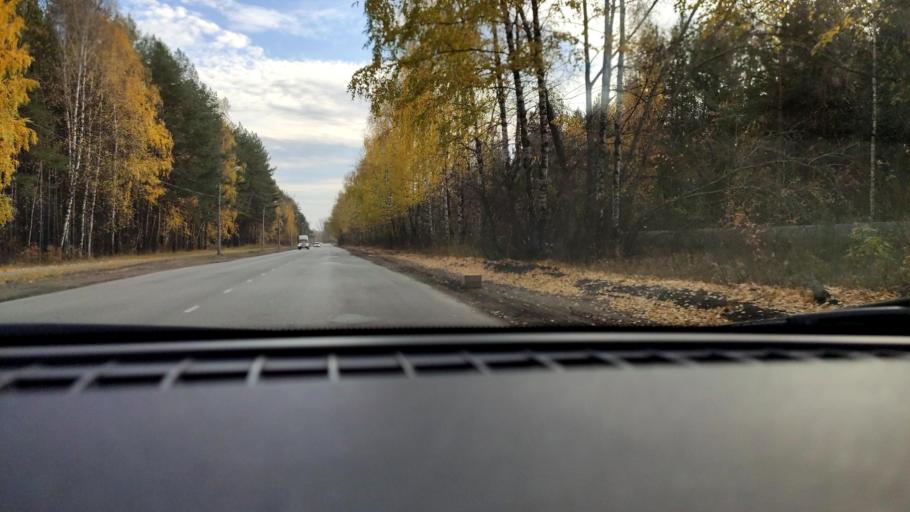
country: RU
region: Perm
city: Overyata
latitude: 58.0139
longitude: 55.9119
